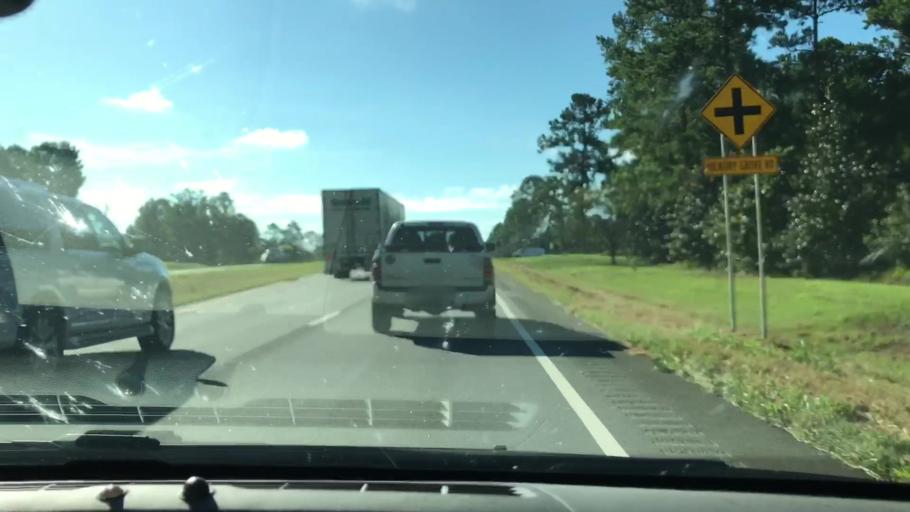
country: US
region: Georgia
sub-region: Lee County
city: Leesburg
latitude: 31.6482
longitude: -84.2613
